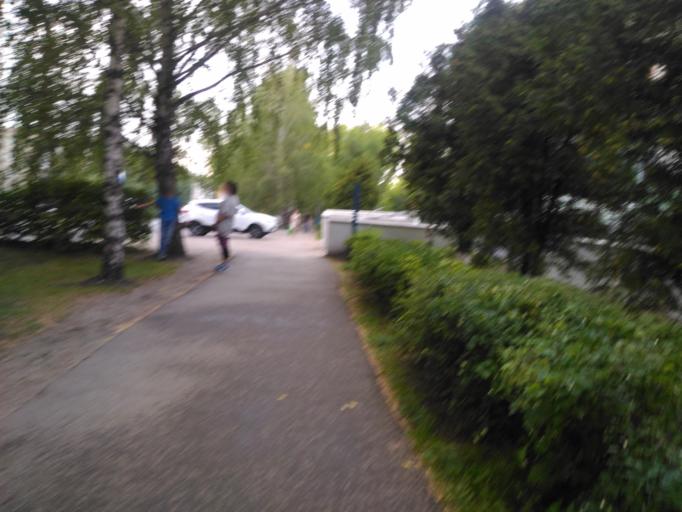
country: RU
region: Ulyanovsk
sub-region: Ulyanovskiy Rayon
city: Ulyanovsk
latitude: 54.2654
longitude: 48.3349
